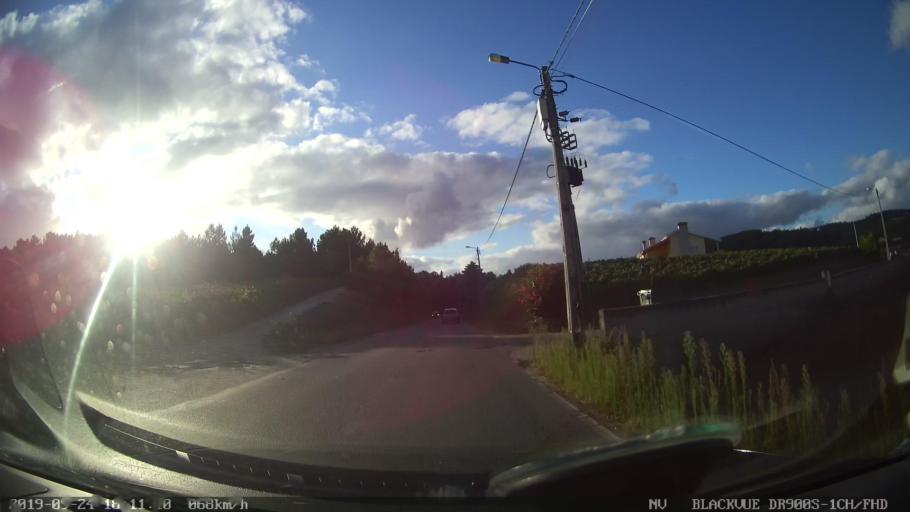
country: PT
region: Vila Real
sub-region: Sabrosa
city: Sabrosa
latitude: 41.2543
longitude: -7.5811
